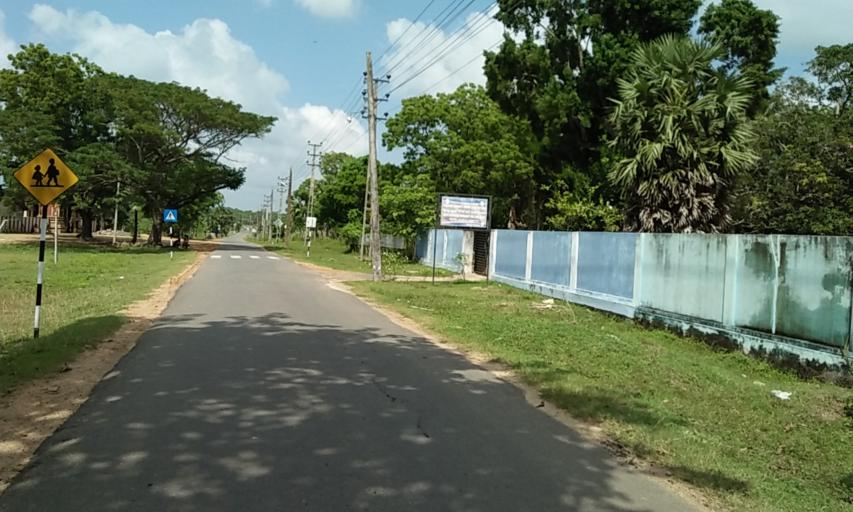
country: LK
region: Eastern Province
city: Ampara
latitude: 7.3372
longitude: 81.7429
